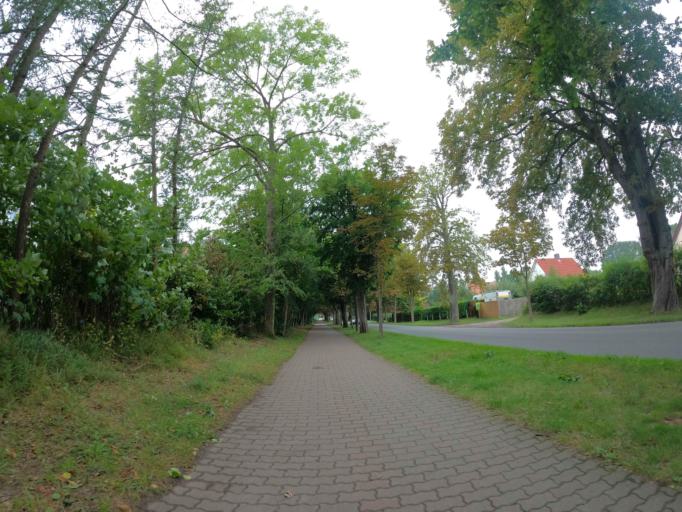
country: DE
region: Mecklenburg-Vorpommern
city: Putbus
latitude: 54.3483
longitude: 13.4883
